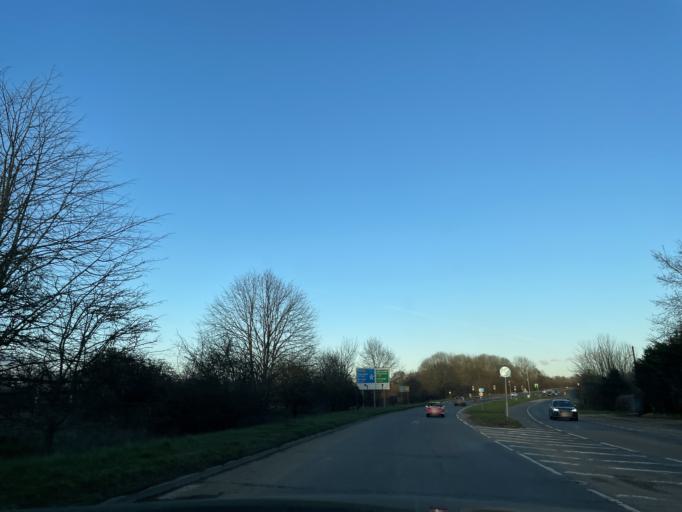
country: GB
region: England
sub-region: Kent
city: Halstead
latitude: 51.2813
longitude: 0.1430
